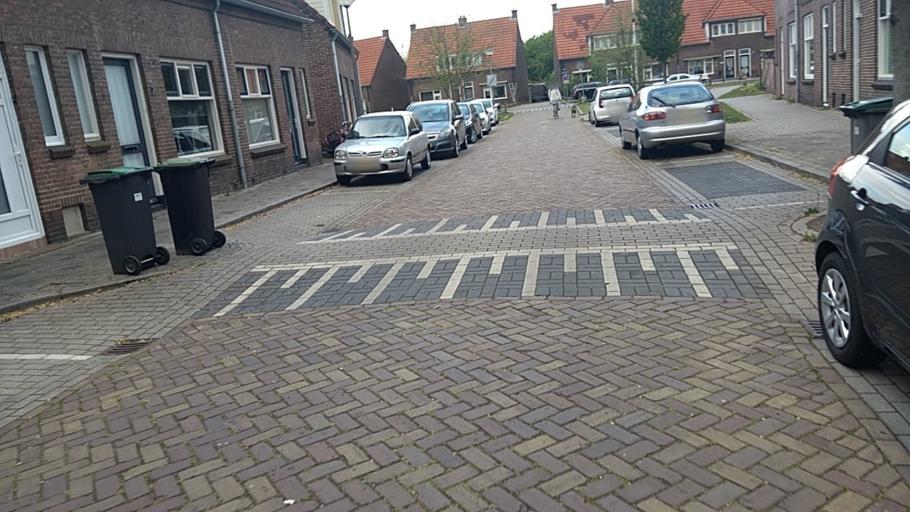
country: NL
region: Overijssel
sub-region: Gemeente Almelo
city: Almelo
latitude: 52.3413
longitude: 6.6673
